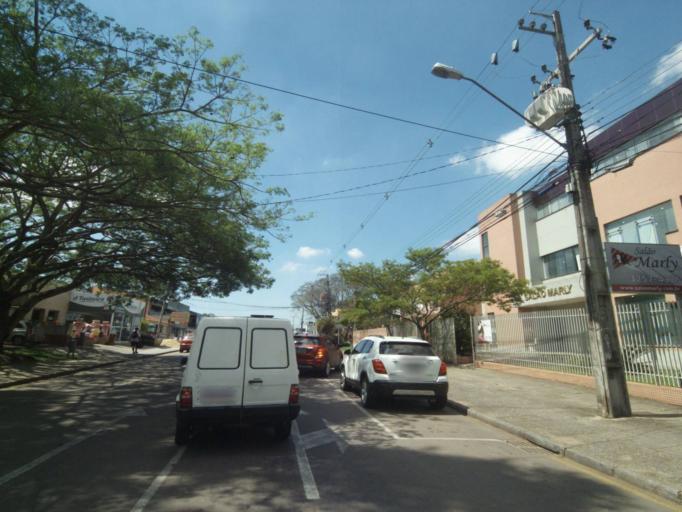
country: BR
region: Parana
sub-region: Curitiba
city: Curitiba
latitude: -25.4021
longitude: -49.2449
